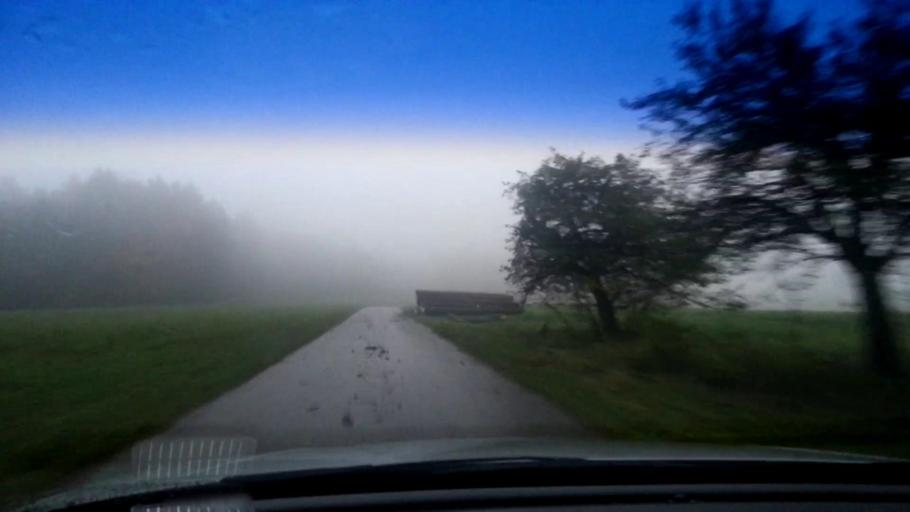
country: DE
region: Bavaria
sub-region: Upper Franconia
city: Schesslitz
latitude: 49.9329
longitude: 11.0648
